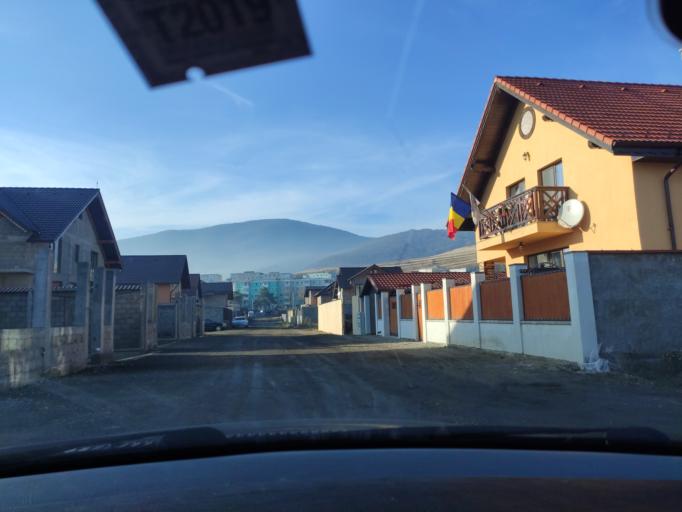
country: RO
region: Brasov
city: Codlea
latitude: 45.7067
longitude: 25.4557
